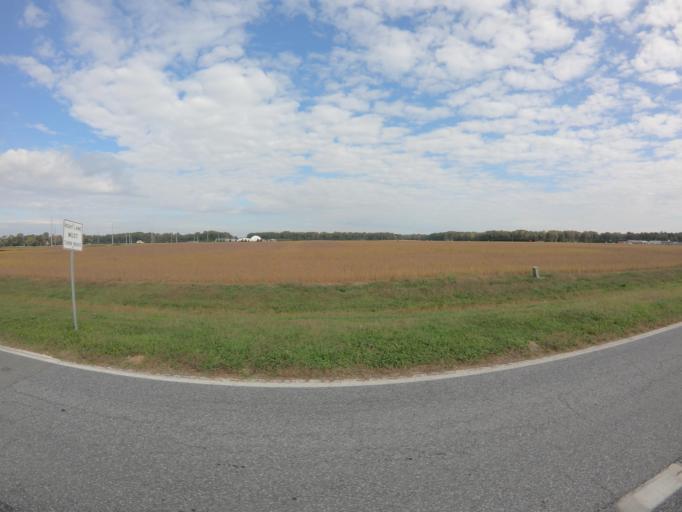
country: US
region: Delaware
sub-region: Sussex County
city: Bridgeville
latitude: 38.7601
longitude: -75.5994
